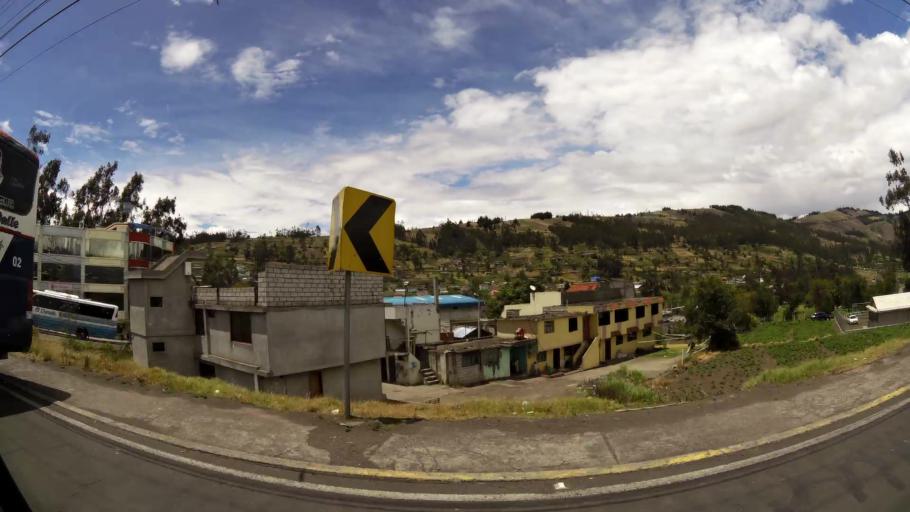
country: EC
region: Tungurahua
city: Pelileo
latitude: -1.3273
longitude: -78.5488
